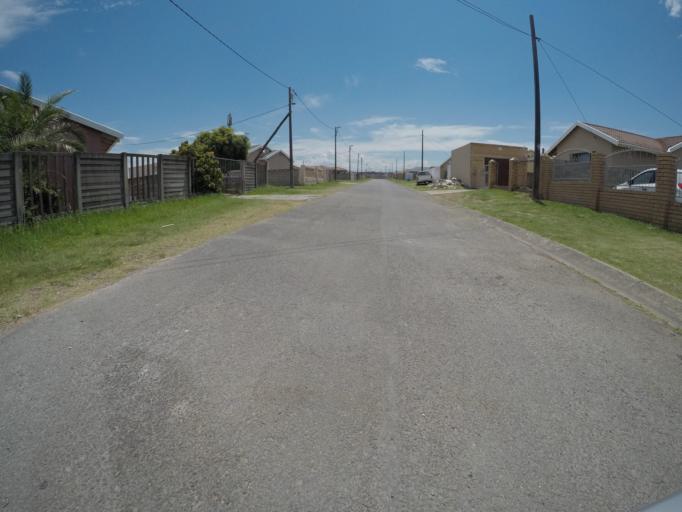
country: ZA
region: Eastern Cape
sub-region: Buffalo City Metropolitan Municipality
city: East London
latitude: -33.0498
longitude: 27.8503
